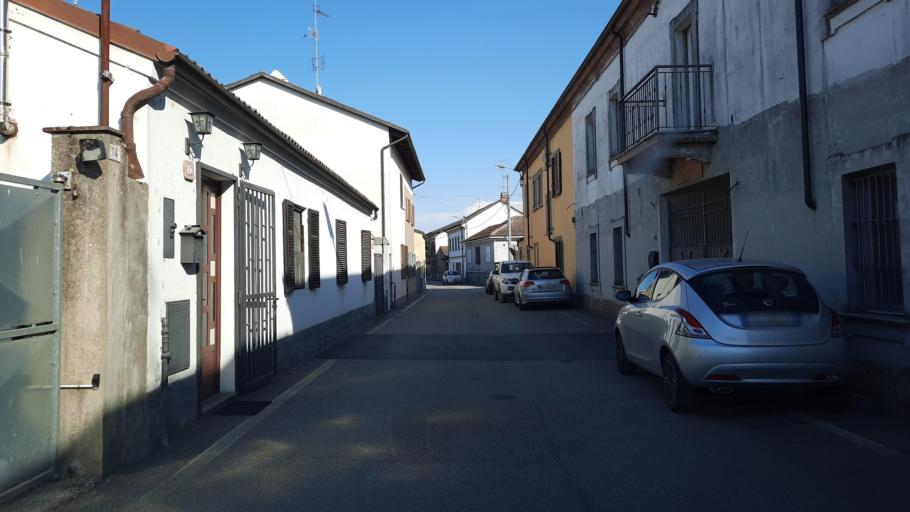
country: IT
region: Piedmont
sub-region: Provincia di Vercelli
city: Lignana
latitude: 45.2852
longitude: 8.3430
